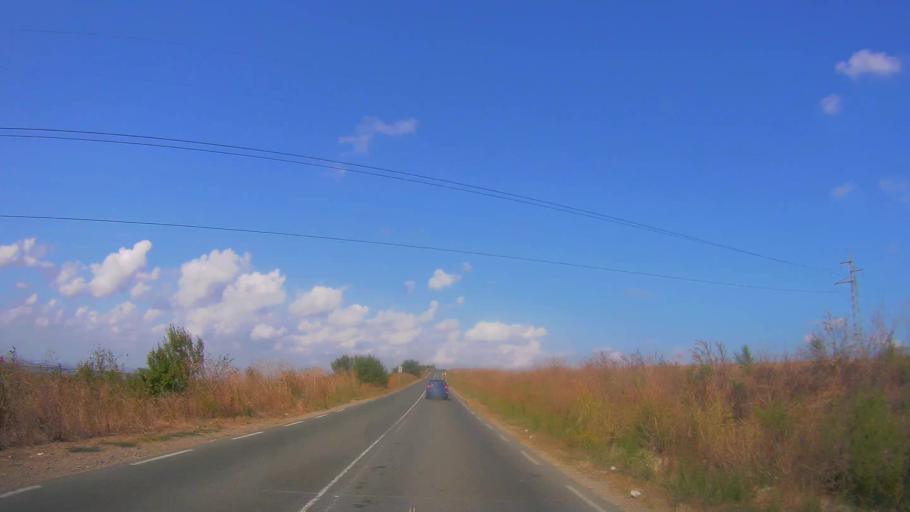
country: BG
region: Burgas
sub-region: Obshtina Burgas
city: Burgas
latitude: 42.4774
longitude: 27.3712
